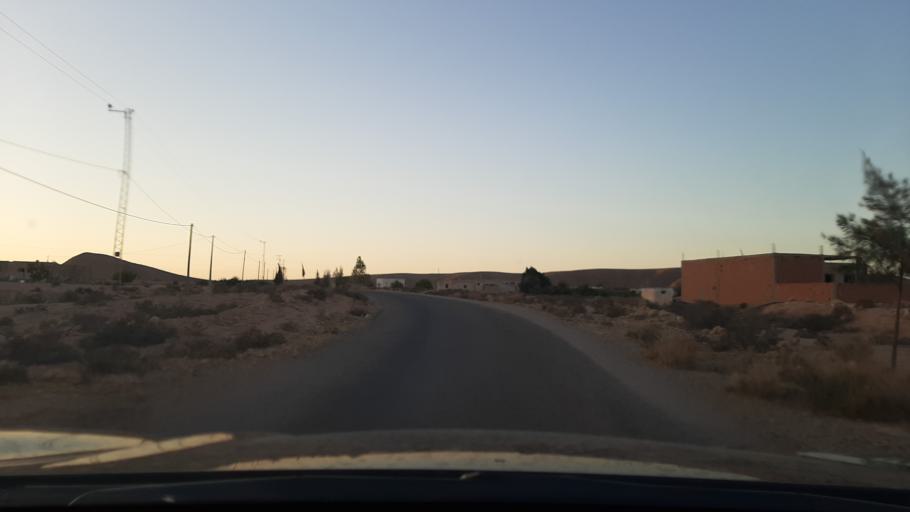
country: TN
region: Qabis
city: Matmata
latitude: 33.5668
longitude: 10.1781
